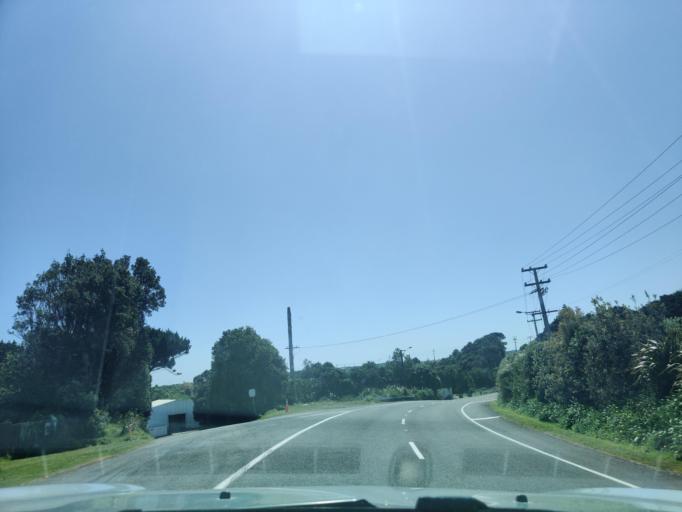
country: NZ
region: Taranaki
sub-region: South Taranaki District
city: Opunake
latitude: -39.4485
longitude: 173.8458
